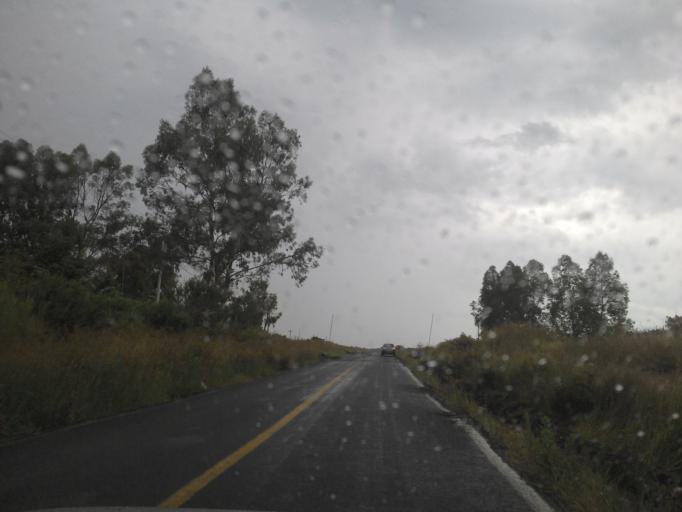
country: MX
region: Jalisco
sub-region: Arandas
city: Santiaguito (Santiaguito de Velazquez)
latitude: 20.7914
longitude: -102.2594
